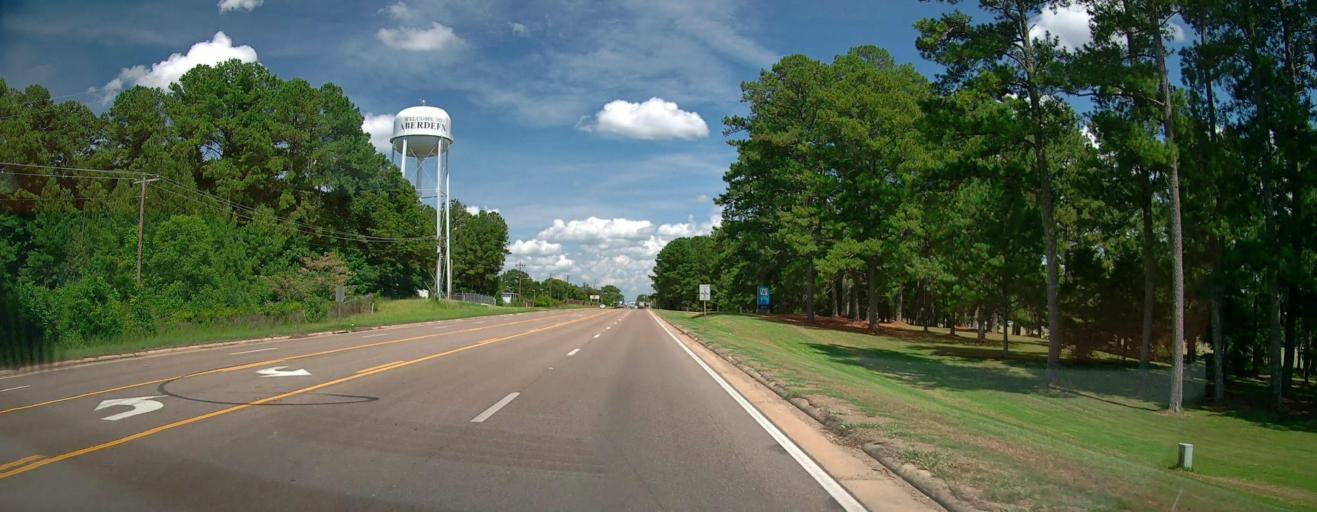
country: US
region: Mississippi
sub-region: Monroe County
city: Aberdeen
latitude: 33.8148
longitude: -88.5599
